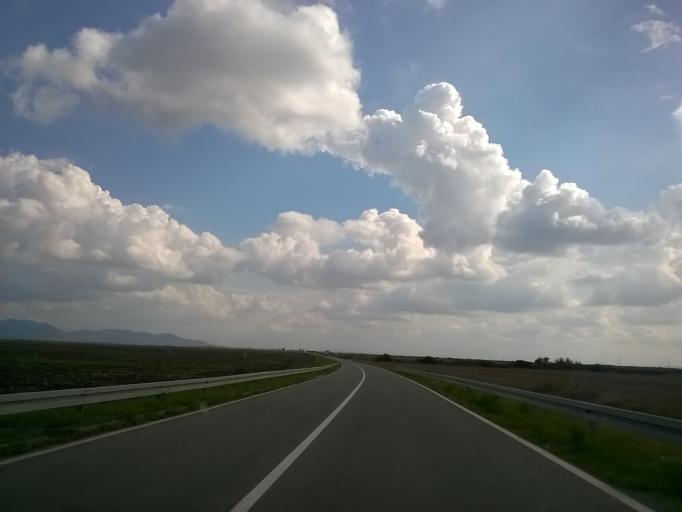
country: RS
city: Margita
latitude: 45.2046
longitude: 21.1830
